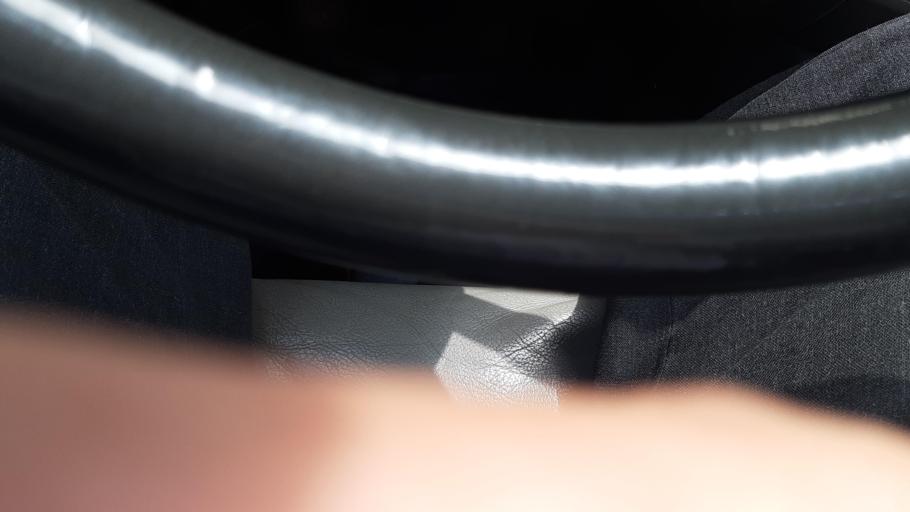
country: LA
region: Vientiane
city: Vientiane
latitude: 18.0394
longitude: 102.6149
